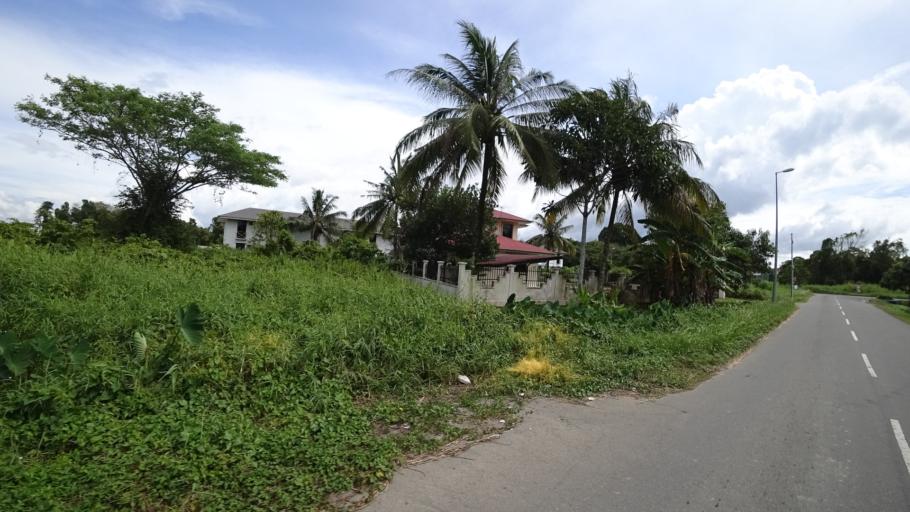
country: BN
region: Brunei and Muara
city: Bandar Seri Begawan
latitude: 4.8925
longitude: 114.8418
